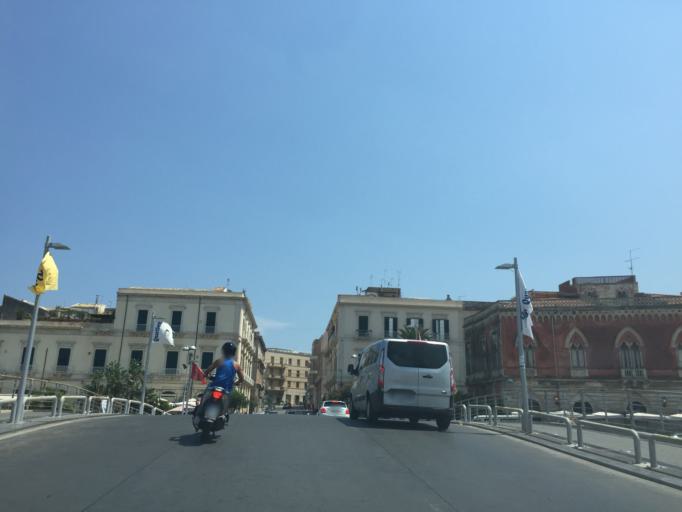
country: IT
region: Sicily
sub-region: Provincia di Siracusa
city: Siracusa
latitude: 37.0643
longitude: 15.2905
